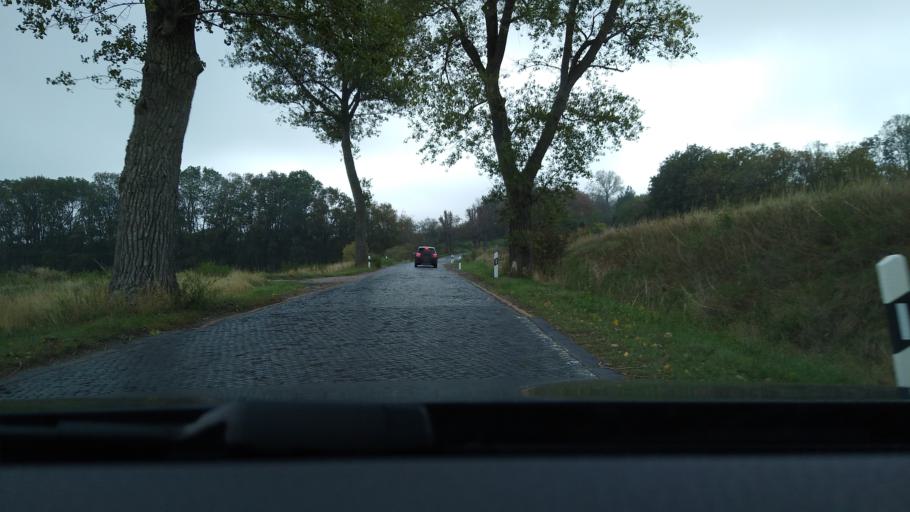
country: DE
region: Saxony-Anhalt
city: Gerbstedt
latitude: 51.6163
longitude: 11.6127
